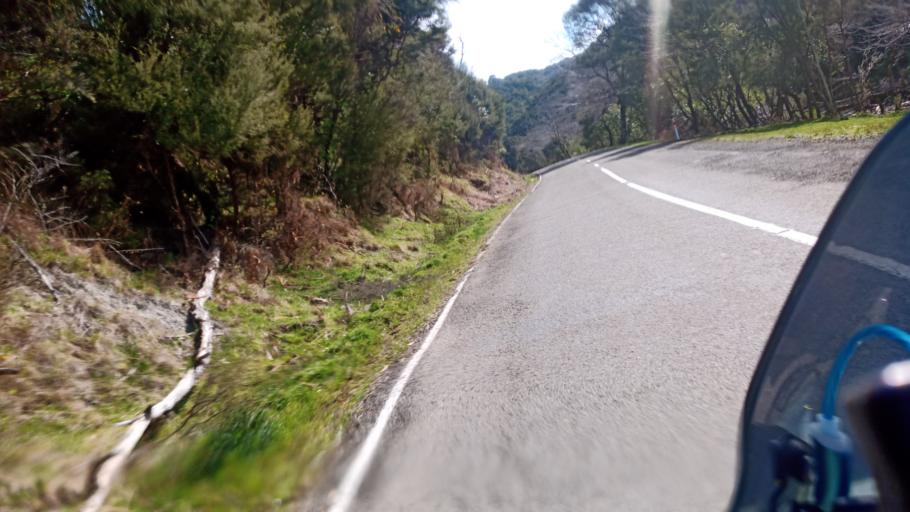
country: NZ
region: Gisborne
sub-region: Gisborne District
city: Gisborne
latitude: -37.8640
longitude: 178.1889
